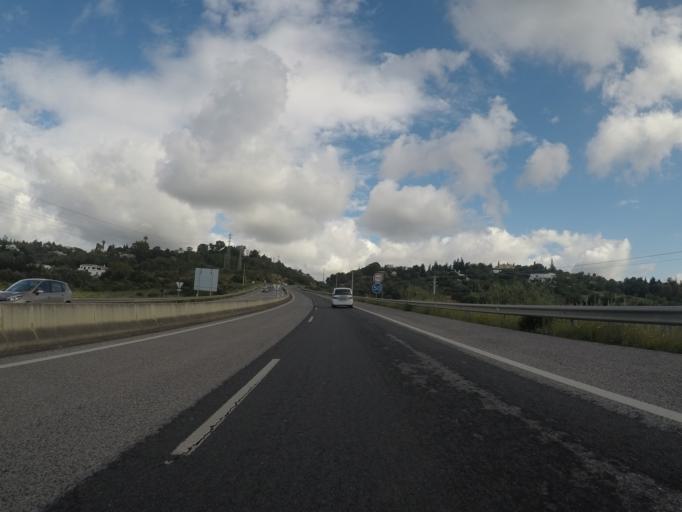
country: PT
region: Faro
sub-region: Lagos
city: Lagos
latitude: 37.1098
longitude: -8.6977
